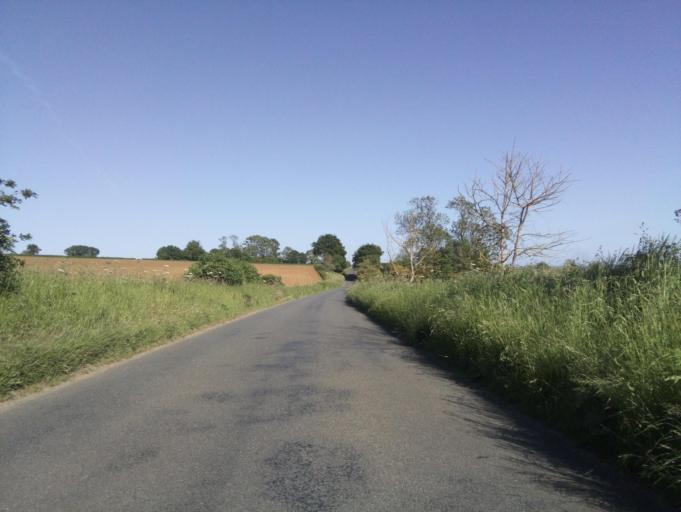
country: GB
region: England
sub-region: Somerset
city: Yeovil
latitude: 50.9358
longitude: -2.5976
